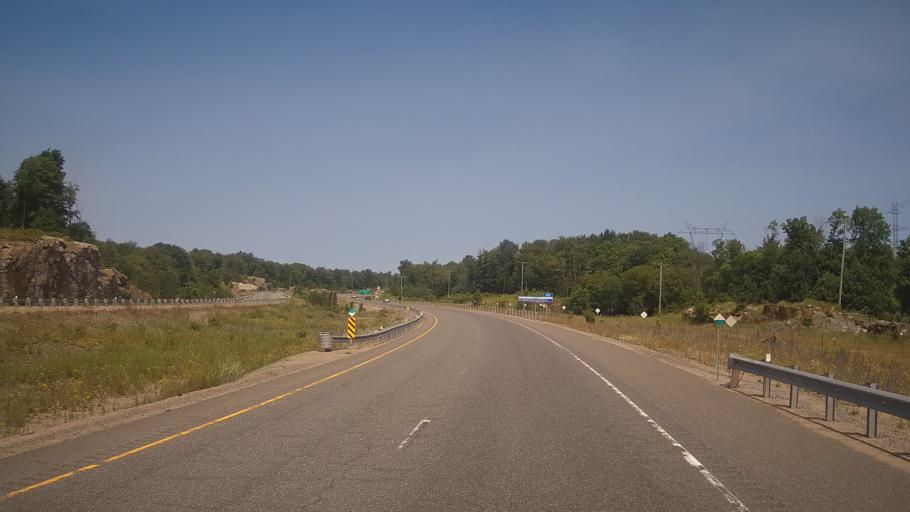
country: CA
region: Ontario
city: Midland
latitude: 45.0415
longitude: -79.7734
